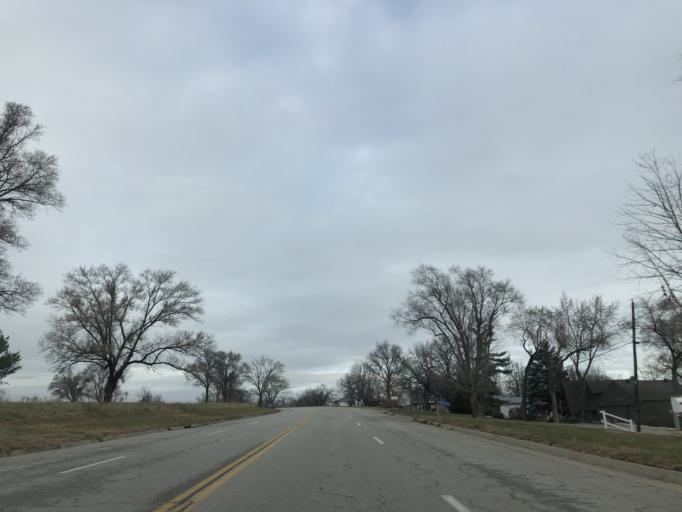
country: US
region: Kansas
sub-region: Johnson County
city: Gardner
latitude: 38.8457
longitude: -94.9298
